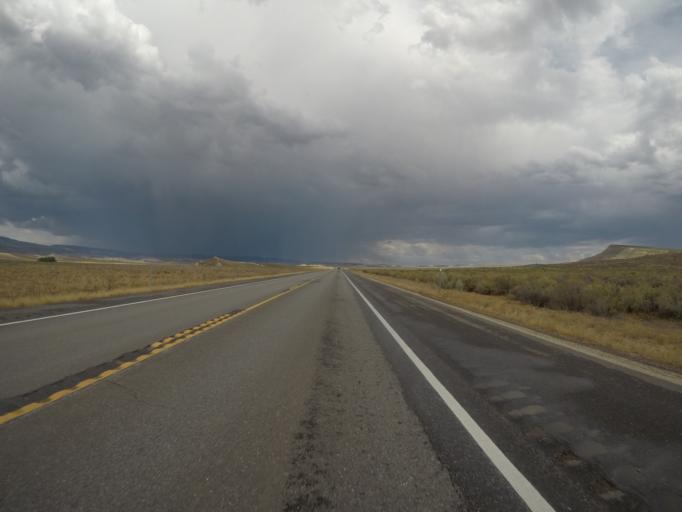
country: US
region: Utah
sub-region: Uintah County
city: Naples
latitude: 40.2876
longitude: -109.1445
